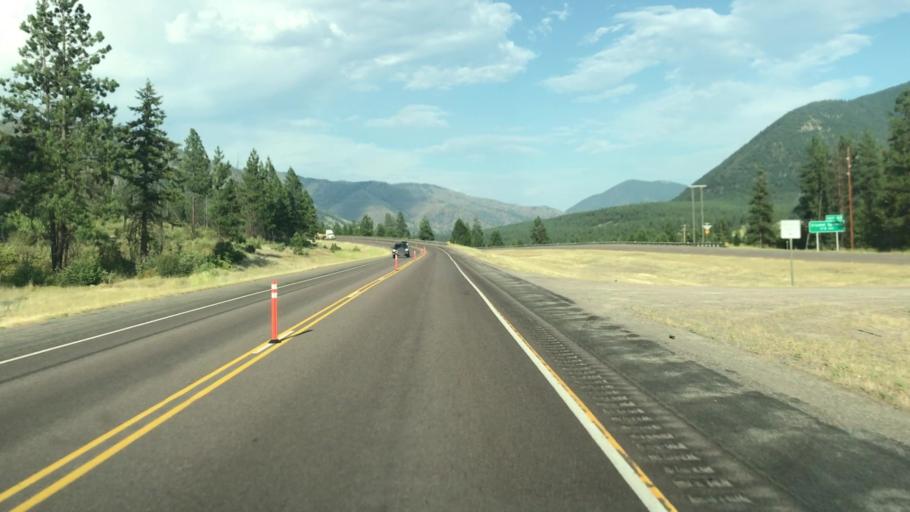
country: US
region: Montana
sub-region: Mineral County
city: Superior
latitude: 47.0132
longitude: -114.6998
